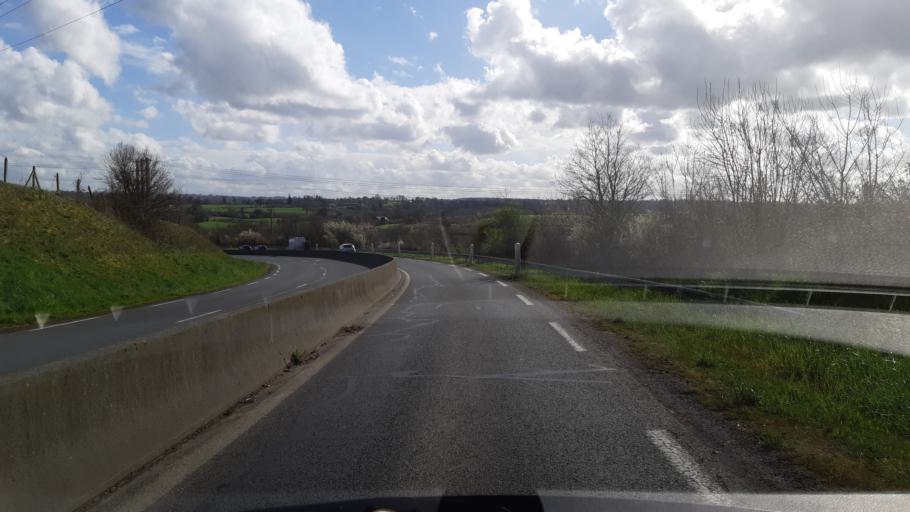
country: FR
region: Lower Normandy
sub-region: Departement de la Manche
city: Agneaux
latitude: 49.0971
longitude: -1.1212
